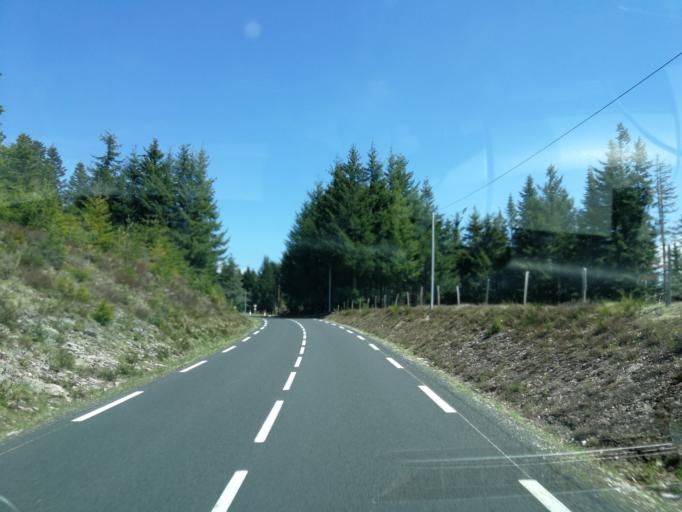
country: FR
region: Rhone-Alpes
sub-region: Departement de l'Ardeche
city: Saint-Agreve
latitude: 45.0866
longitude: 4.3914
